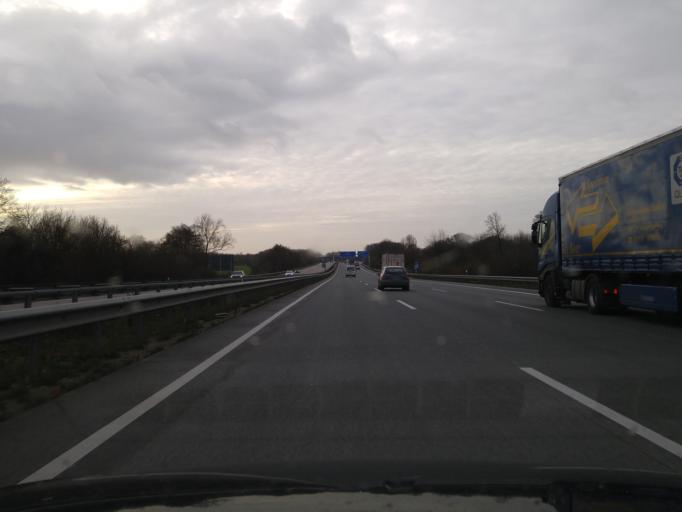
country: DE
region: Schleswig-Holstein
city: Lasbek
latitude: 53.7255
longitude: 10.3448
